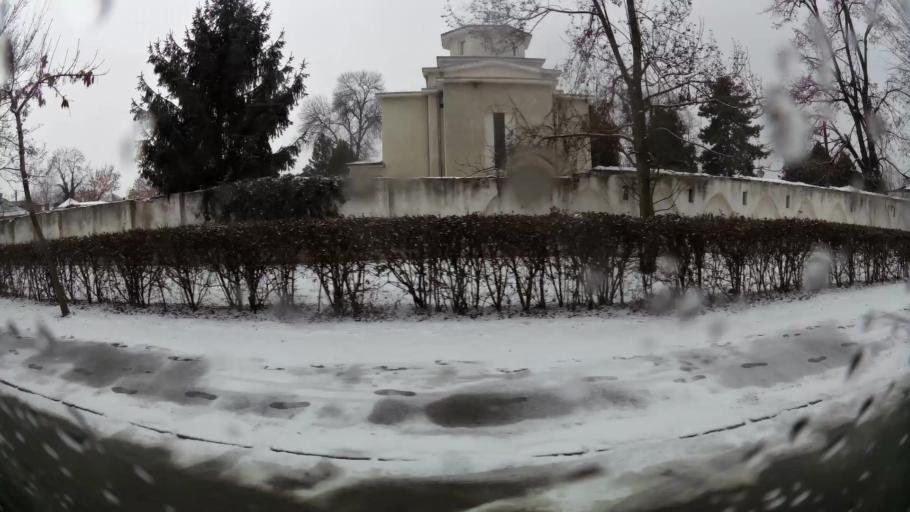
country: RO
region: Prahova
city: Ploiesti
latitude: 44.9265
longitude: 26.0114
